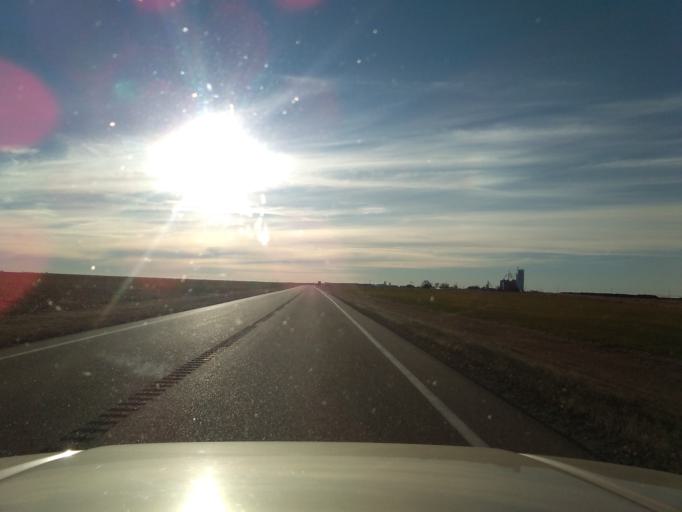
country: US
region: Kansas
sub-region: Thomas County
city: Colby
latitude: 39.4520
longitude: -100.8038
